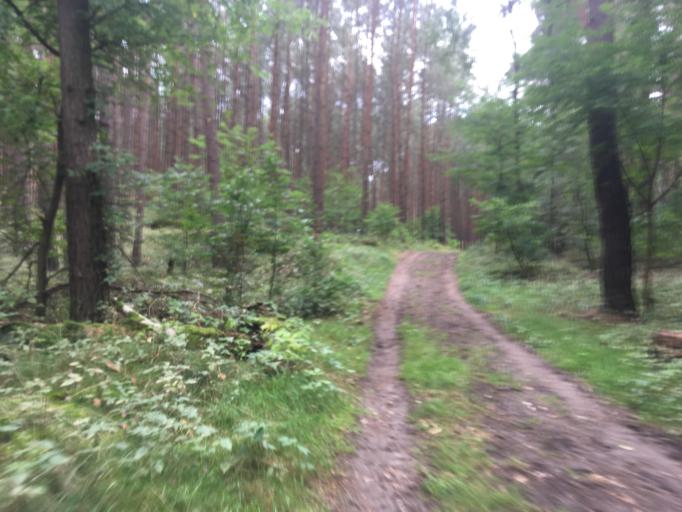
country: DE
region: Brandenburg
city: Glienicke
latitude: 52.6779
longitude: 13.3465
